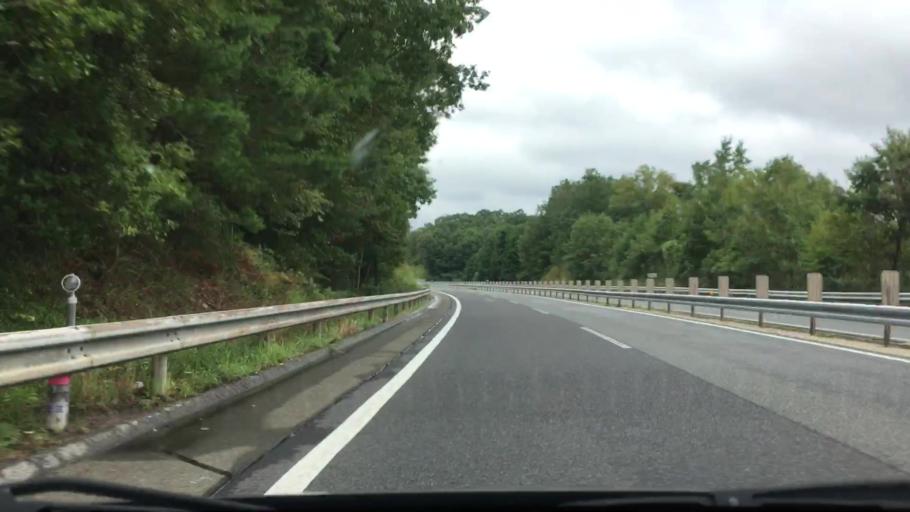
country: JP
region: Hiroshima
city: Shobara
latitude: 34.8388
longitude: 133.0436
